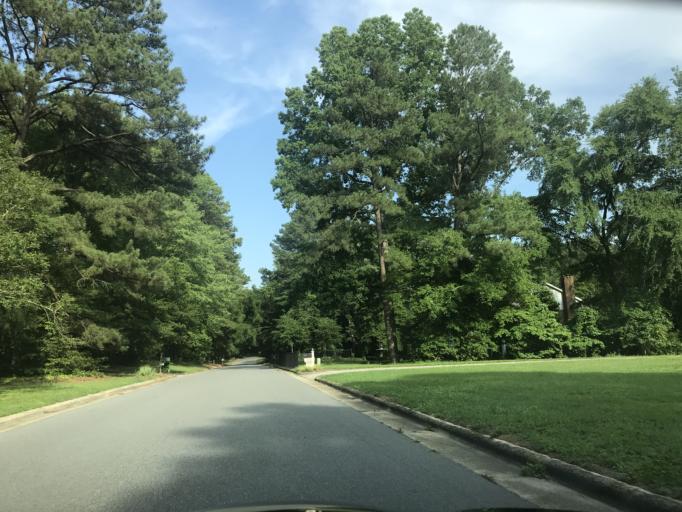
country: US
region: North Carolina
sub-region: Wake County
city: Knightdale
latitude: 35.8330
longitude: -78.5470
